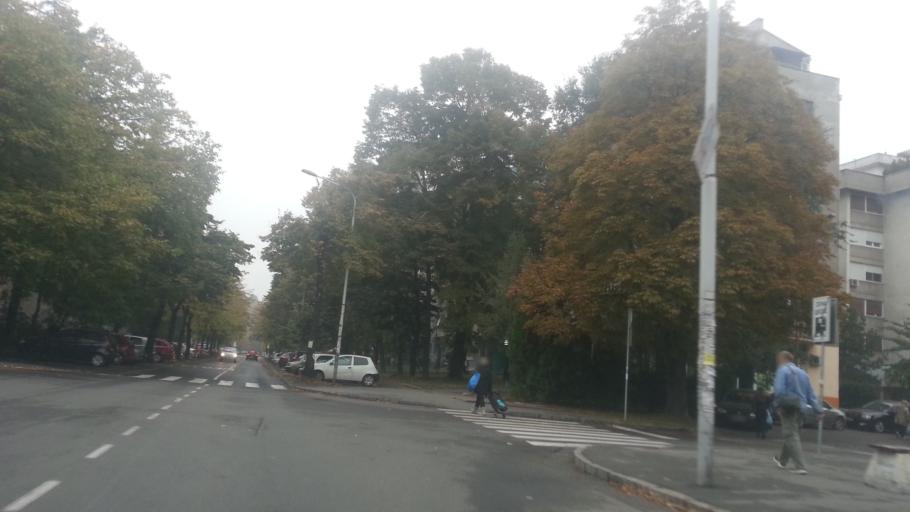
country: RS
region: Central Serbia
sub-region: Belgrade
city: Zemun
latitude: 44.8332
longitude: 20.4077
